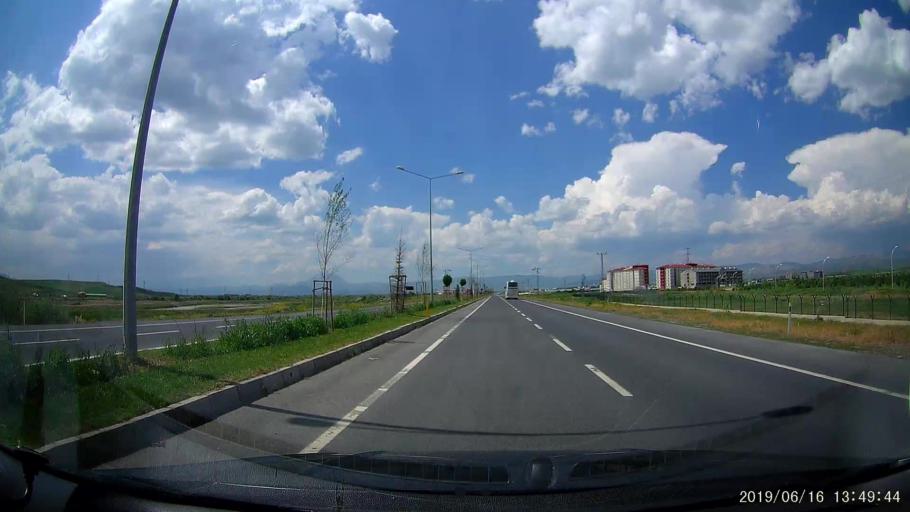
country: TR
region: Agri
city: Agri
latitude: 39.7198
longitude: 42.9871
